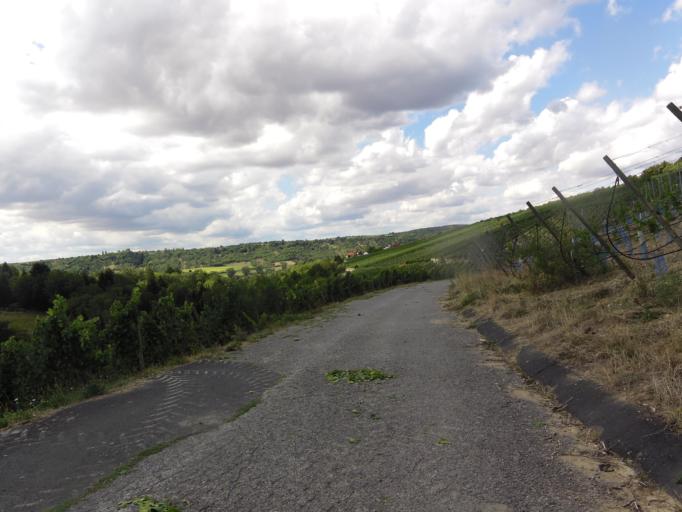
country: DE
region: Bavaria
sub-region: Regierungsbezirk Unterfranken
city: Winterhausen
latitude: 49.7225
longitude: 10.0205
